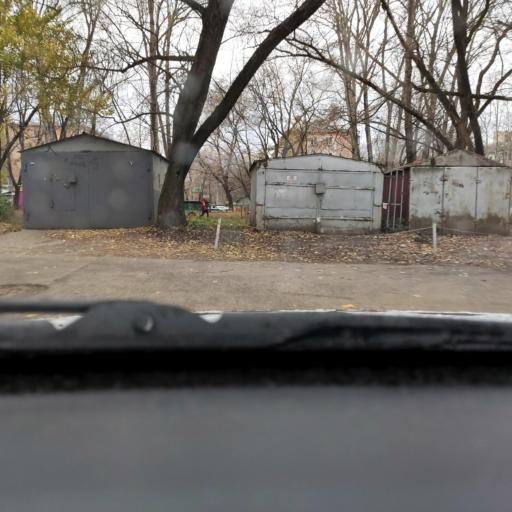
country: RU
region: Perm
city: Perm
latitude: 57.9810
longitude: 56.1926
